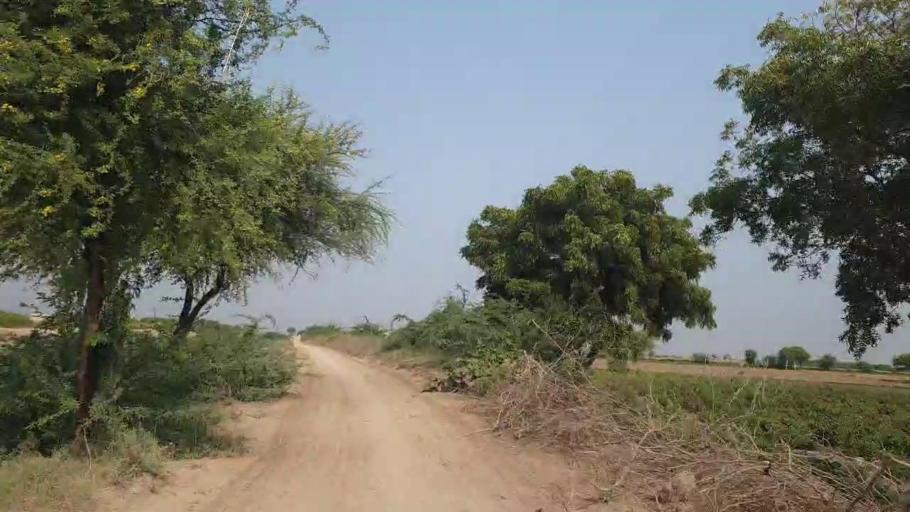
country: PK
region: Sindh
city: Badin
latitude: 24.7009
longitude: 68.7770
